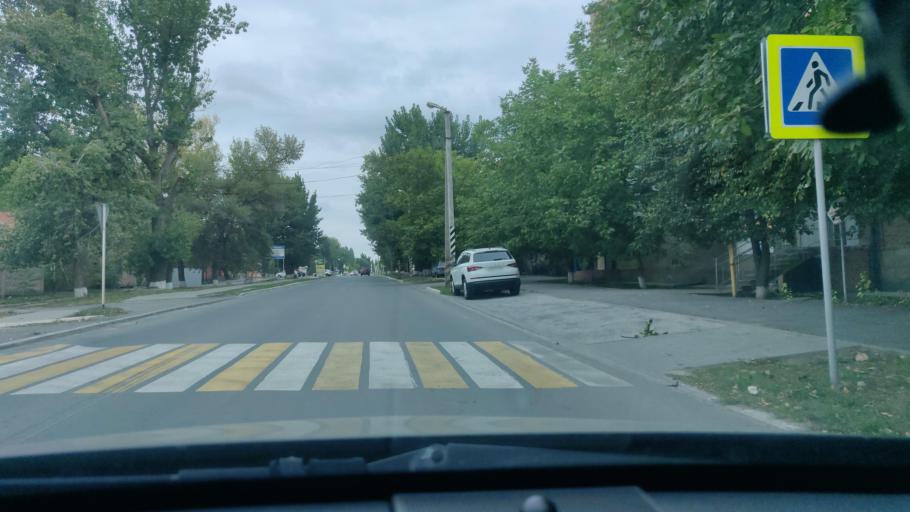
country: RU
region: Rostov
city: Ust'-Donetskiy
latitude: 47.6452
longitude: 40.8610
